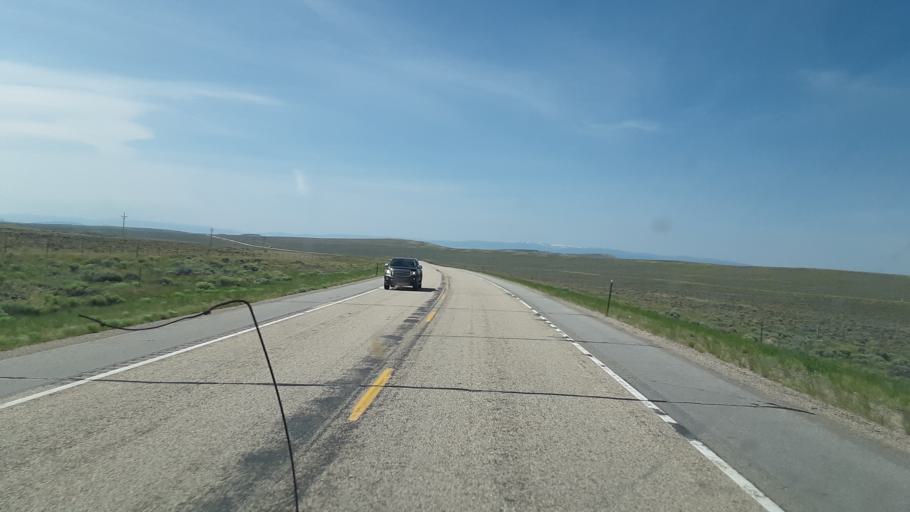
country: US
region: Wyoming
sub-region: Carbon County
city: Saratoga
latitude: 41.6110
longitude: -106.8166
